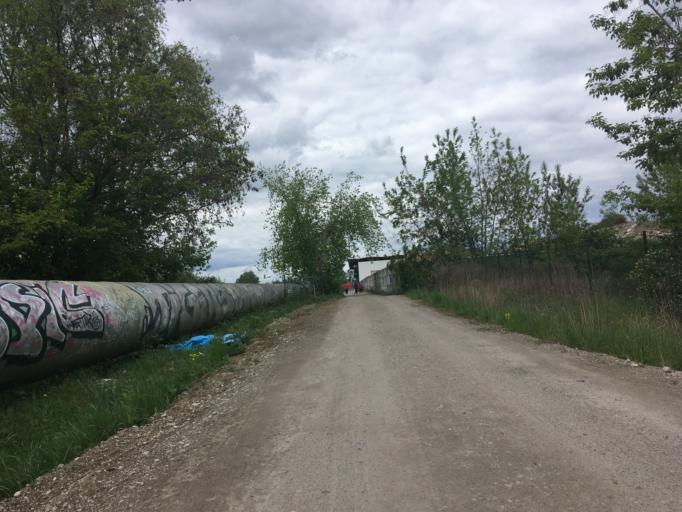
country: DE
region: Berlin
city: Neu-Hohenschoenhausen
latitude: 52.5517
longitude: 13.5294
